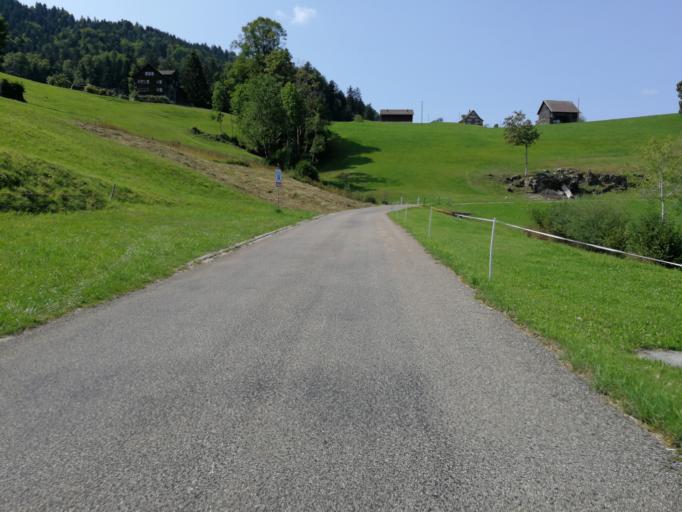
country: CH
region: Saint Gallen
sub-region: Wahlkreis Toggenburg
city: Krummenau
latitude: 47.2465
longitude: 9.1522
